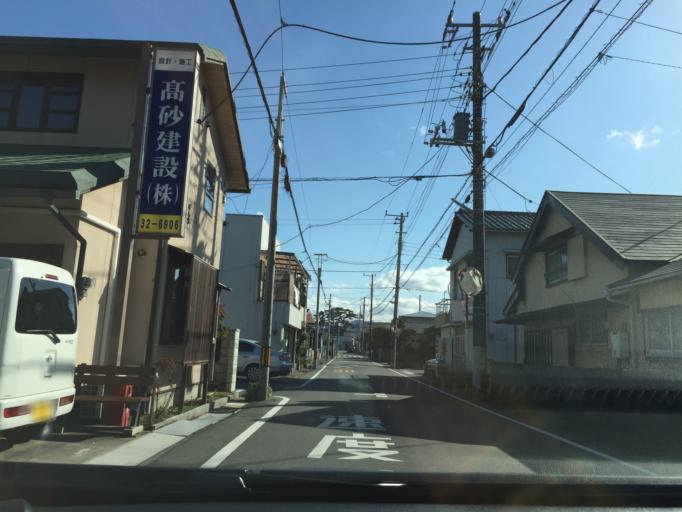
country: JP
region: Shizuoka
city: Numazu
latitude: 35.0784
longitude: 138.8620
